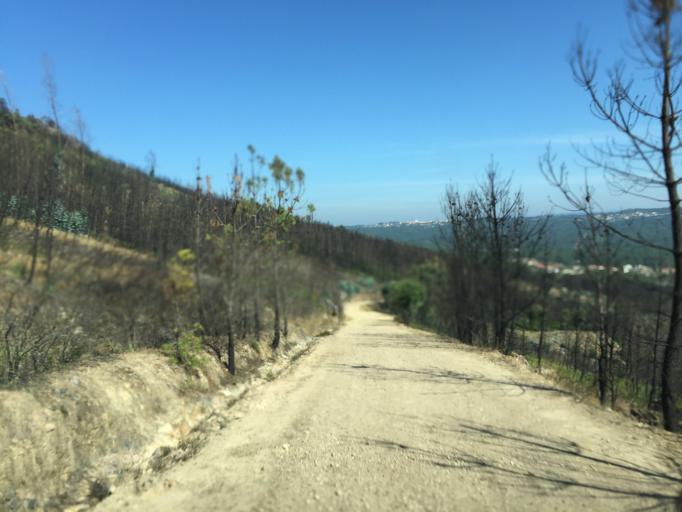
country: PT
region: Santarem
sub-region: Macao
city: Macao
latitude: 39.6568
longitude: -7.9835
